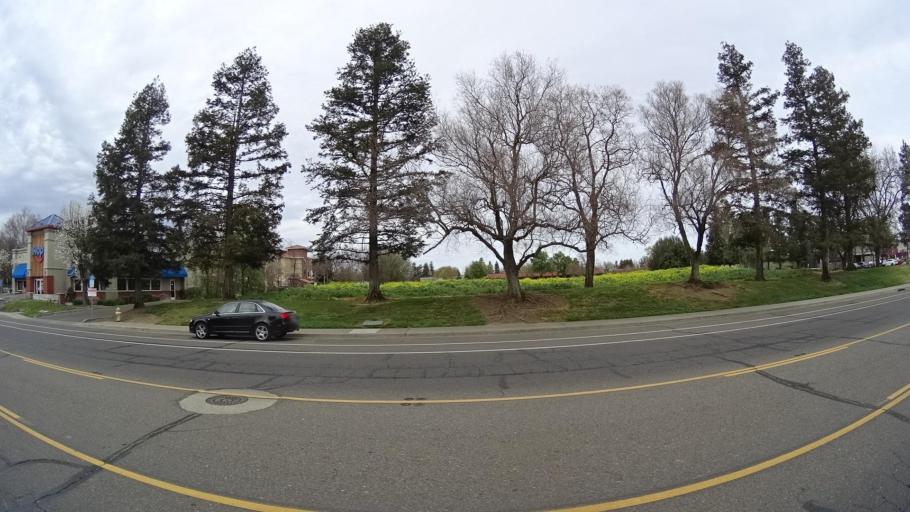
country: US
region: California
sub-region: Yolo County
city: Davis
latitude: 38.5398
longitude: -121.7302
